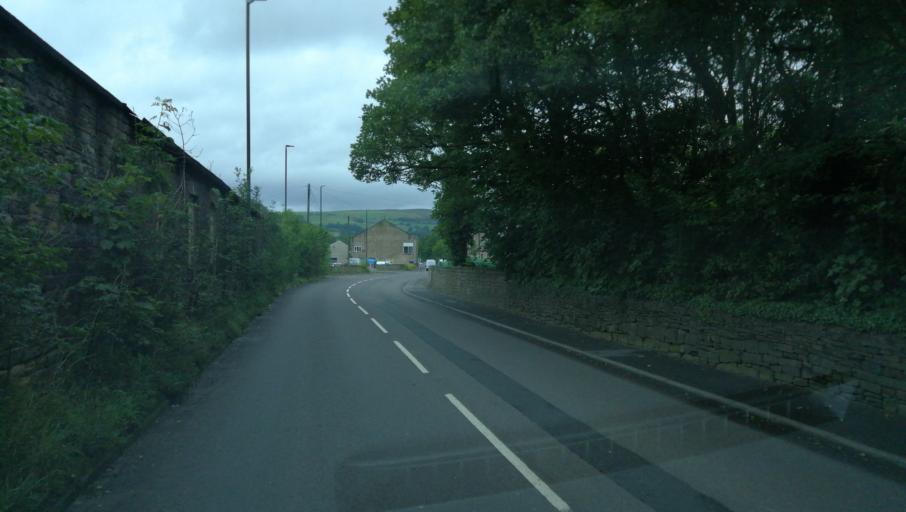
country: GB
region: England
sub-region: Derbyshire
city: Glossop
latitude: 53.4486
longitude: -1.9768
